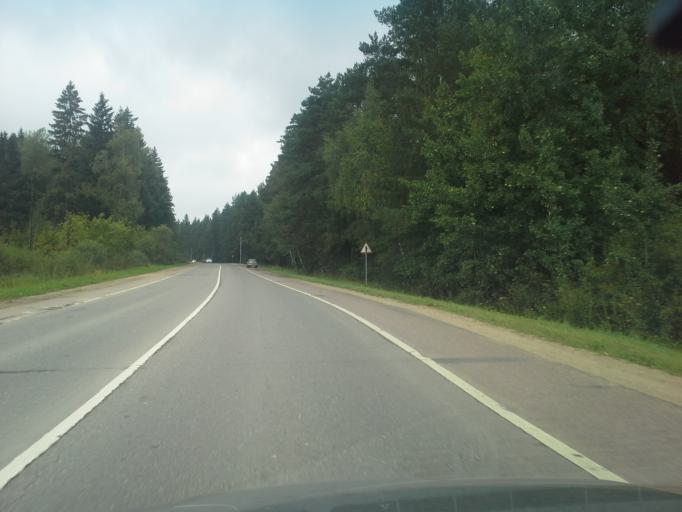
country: RU
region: Moskovskaya
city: Chupryakovo
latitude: 55.5728
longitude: 36.6301
